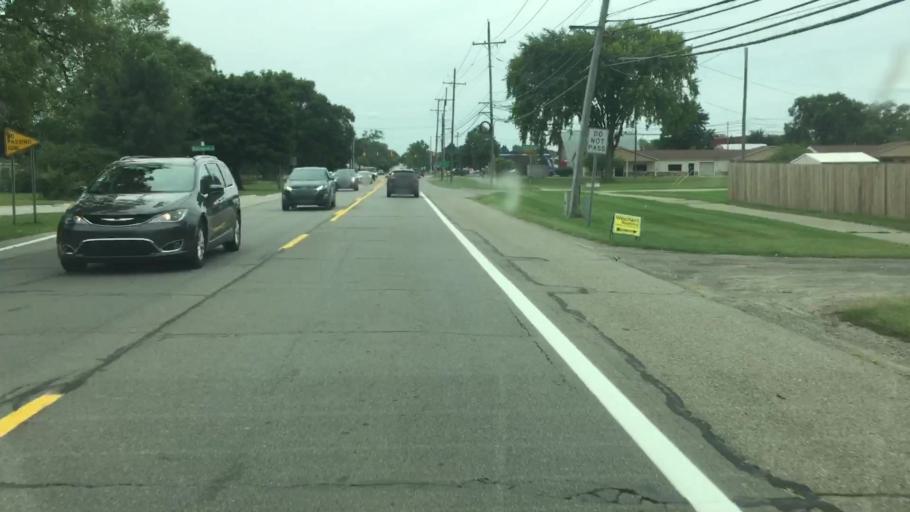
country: US
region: Michigan
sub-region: Oakland County
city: Rochester Hills
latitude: 42.6368
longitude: -83.1086
